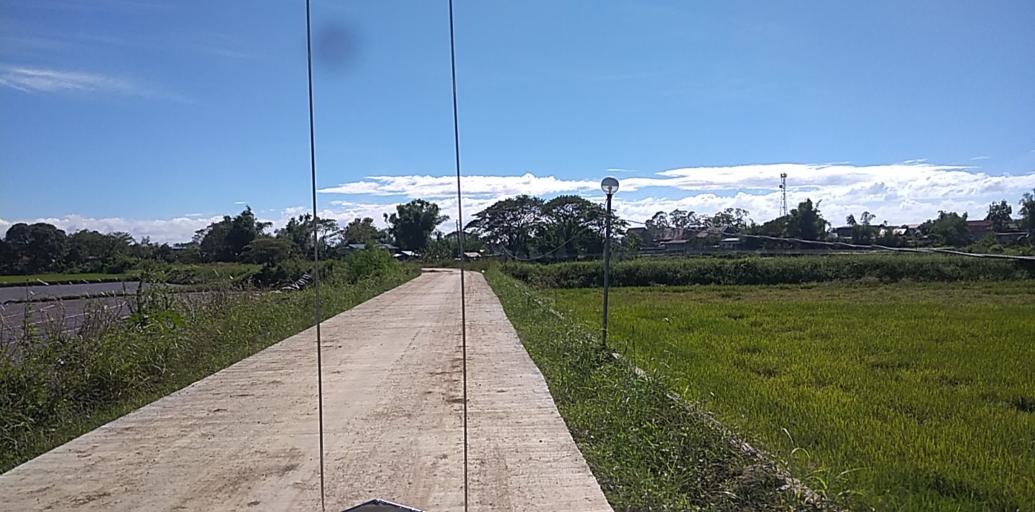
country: PH
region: Central Luzon
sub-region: Province of Pampanga
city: San Nicolas
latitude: 15.0650
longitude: 120.8069
